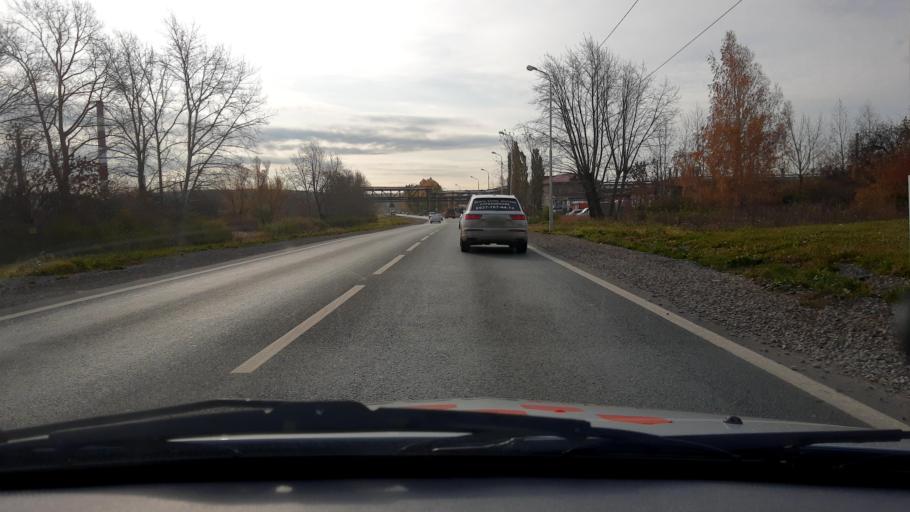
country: RU
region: Bashkortostan
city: Ufa
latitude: 54.8490
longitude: 56.1183
